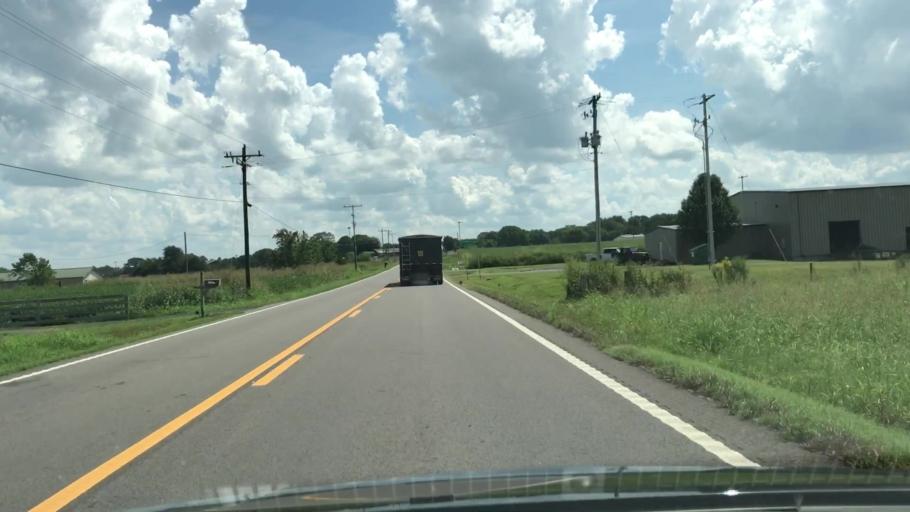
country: US
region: Tennessee
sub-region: Robertson County
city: Springfield
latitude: 36.6046
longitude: -86.9237
